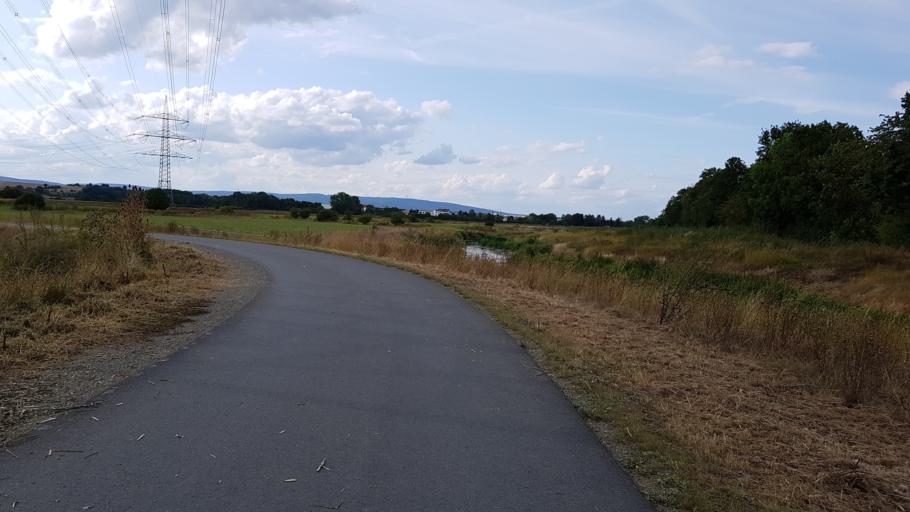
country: DE
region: Hesse
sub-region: Regierungsbezirk Darmstadt
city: Karben
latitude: 50.2148
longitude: 8.7718
